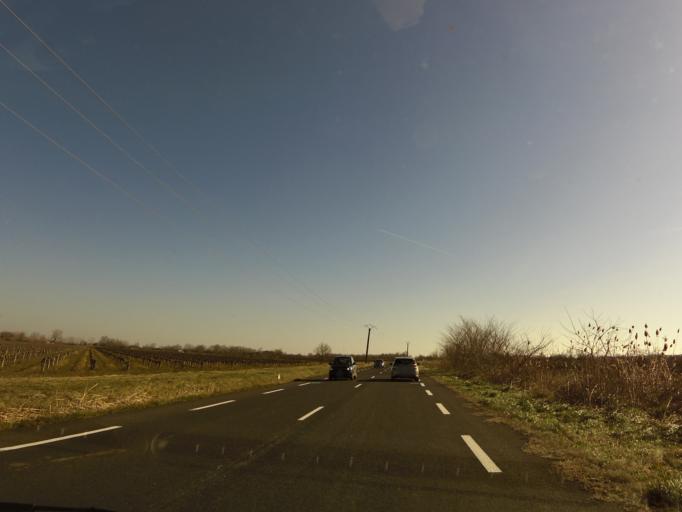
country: FR
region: Languedoc-Roussillon
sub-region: Departement du Gard
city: Aigues-Mortes
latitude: 43.5660
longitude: 4.3132
